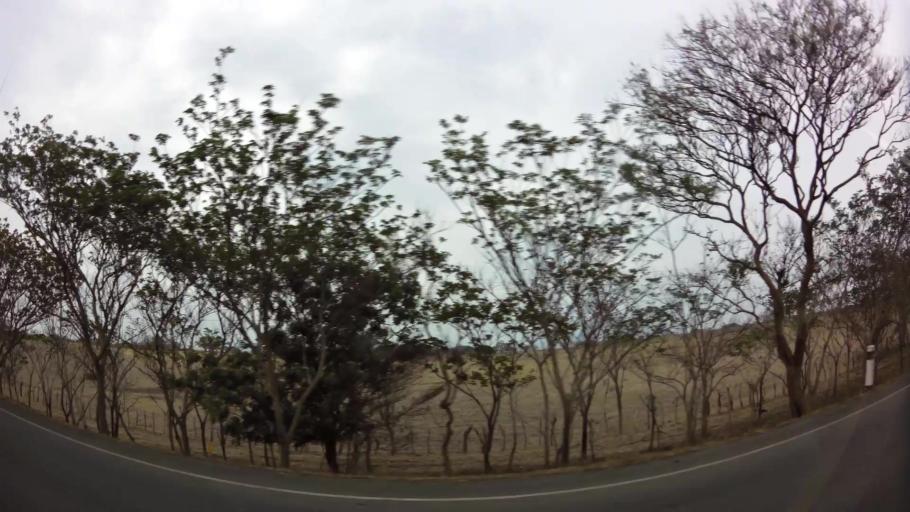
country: NI
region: Rivas
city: San Jorge
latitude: 11.3274
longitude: -85.7183
